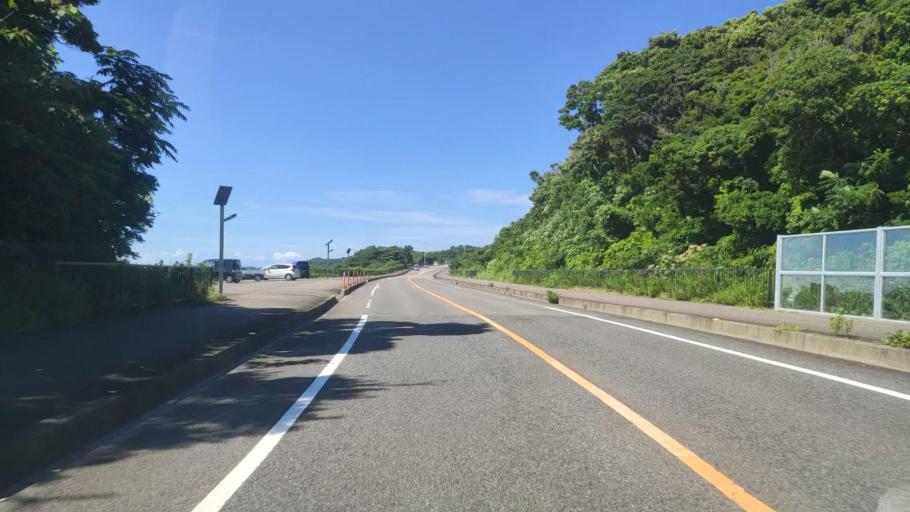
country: JP
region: Wakayama
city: Shingu
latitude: 33.7137
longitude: 136.0001
